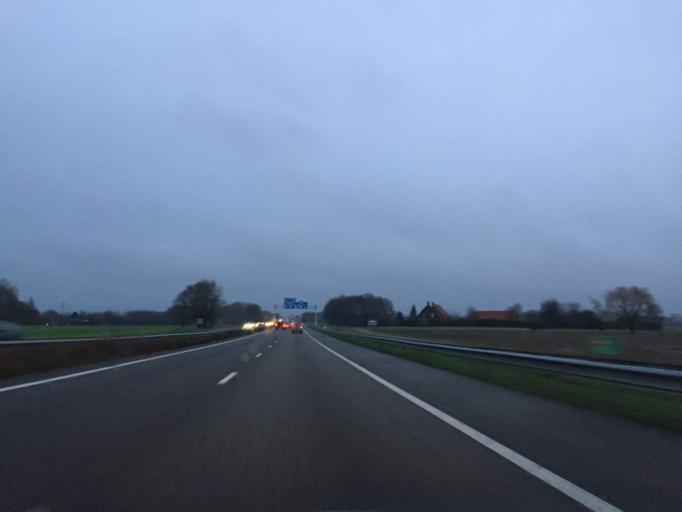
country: NL
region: North Brabant
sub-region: Roosendaal
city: Roosendaal
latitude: 51.5201
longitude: 4.4221
